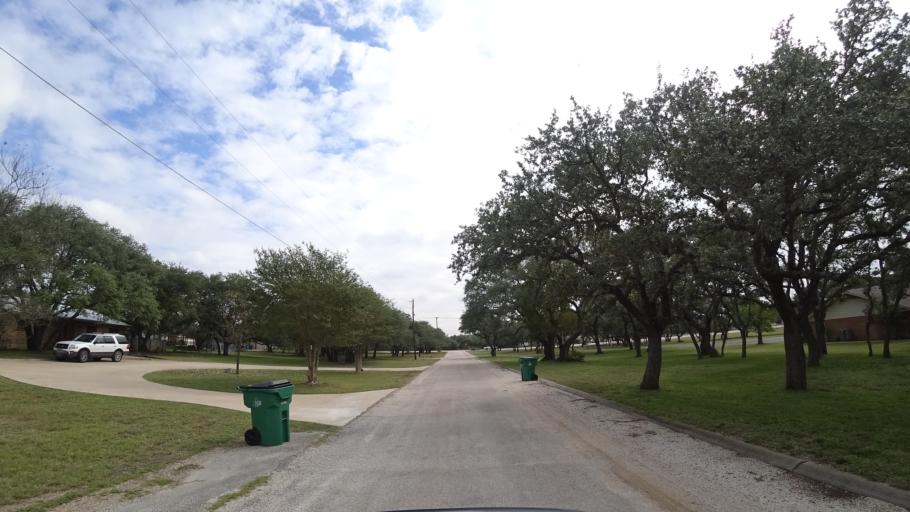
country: US
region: Texas
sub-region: Travis County
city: Shady Hollow
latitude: 30.2122
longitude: -97.8997
